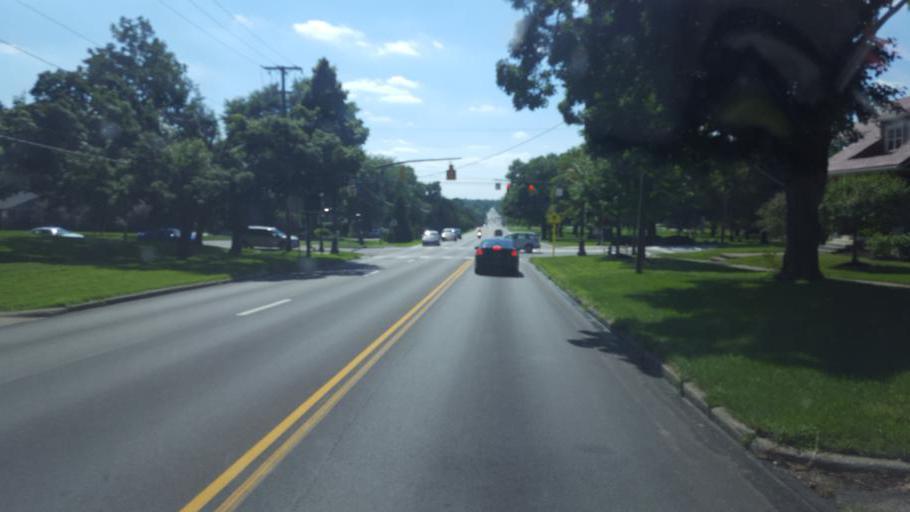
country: US
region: Ohio
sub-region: Franklin County
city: Worthington
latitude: 40.0891
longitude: -83.0215
